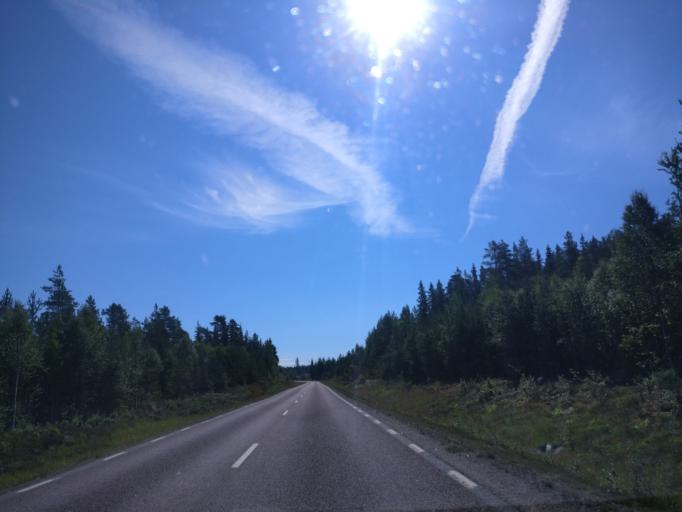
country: SE
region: Vaermland
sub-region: Filipstads Kommun
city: Lesjofors
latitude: 60.0494
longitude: 14.0218
